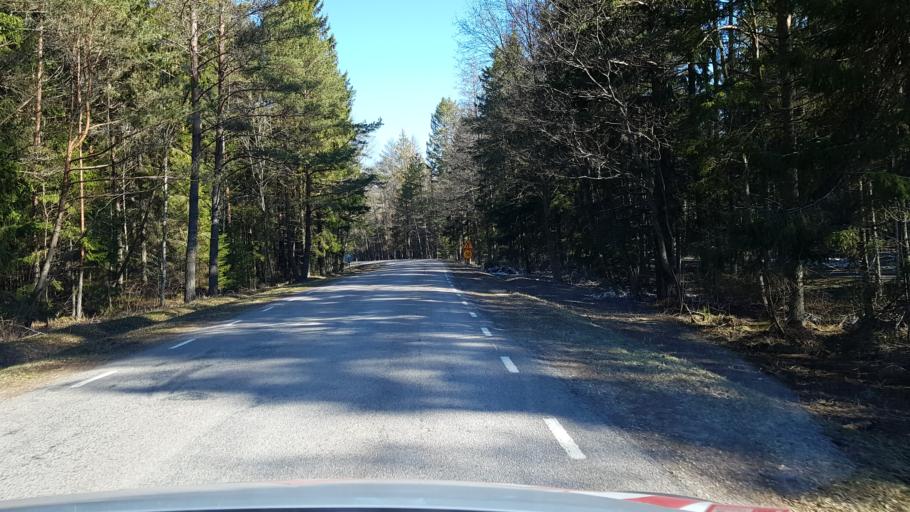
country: EE
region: Harju
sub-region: Loksa linn
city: Loksa
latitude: 59.5889
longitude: 25.9082
